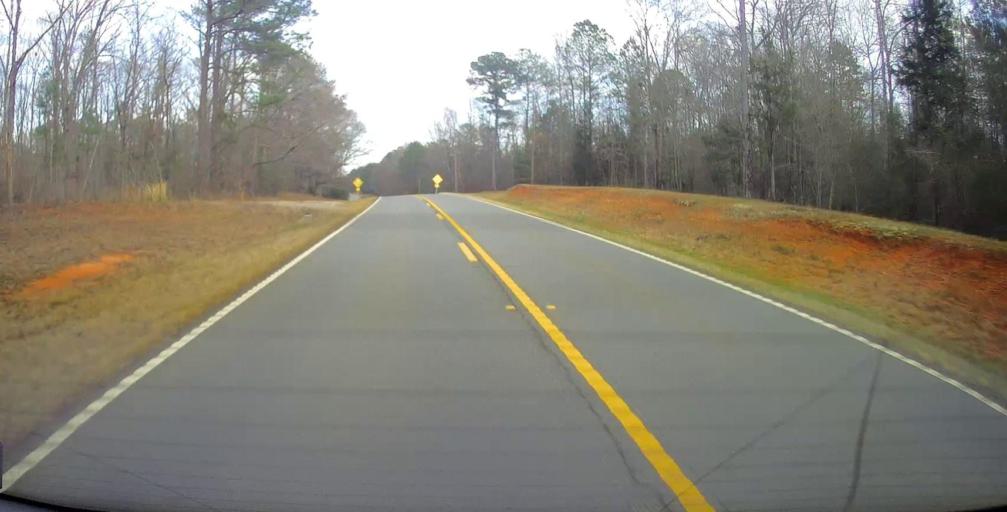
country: US
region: Georgia
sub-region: Harris County
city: Hamilton
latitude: 32.7017
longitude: -84.8368
